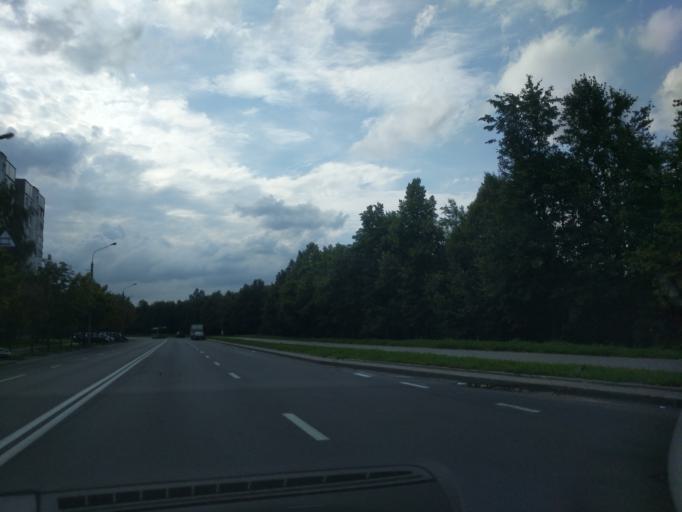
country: BY
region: Minsk
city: Malinovka
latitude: 53.8542
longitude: 27.4721
